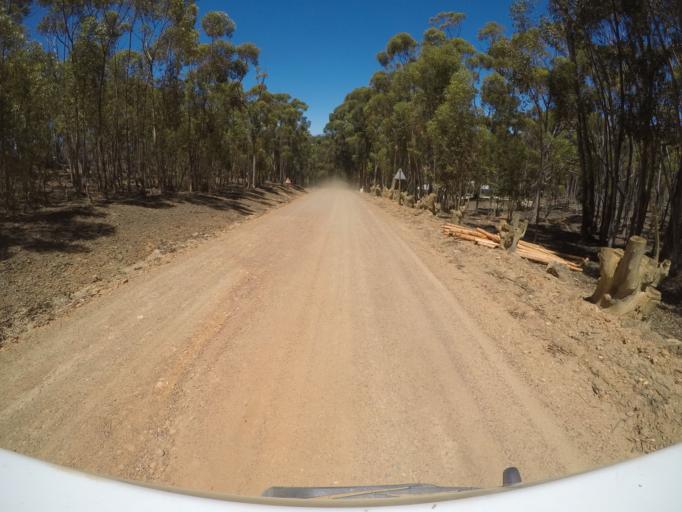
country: ZA
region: Western Cape
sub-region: Overberg District Municipality
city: Grabouw
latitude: -34.1673
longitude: 19.2246
